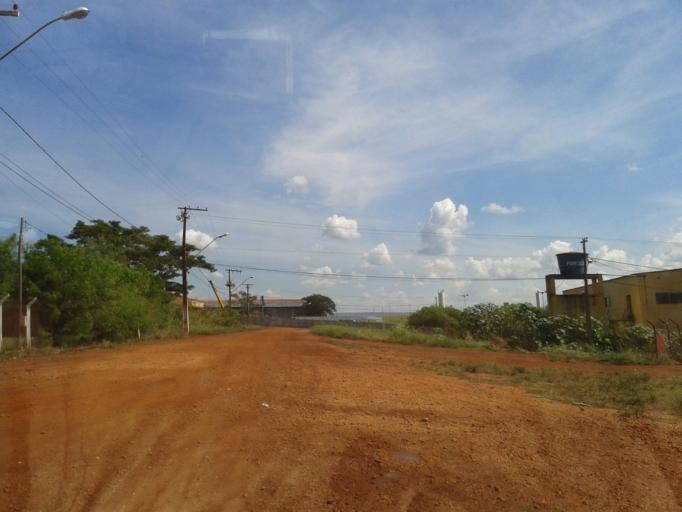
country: BR
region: Goias
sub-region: Itumbiara
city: Itumbiara
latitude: -18.4266
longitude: -49.1903
